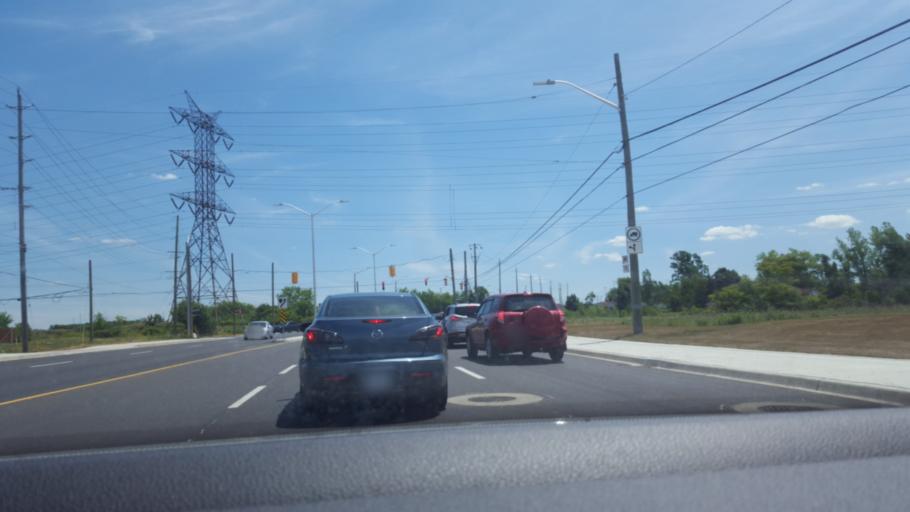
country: CA
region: Ontario
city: Hamilton
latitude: 43.1856
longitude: -79.8237
